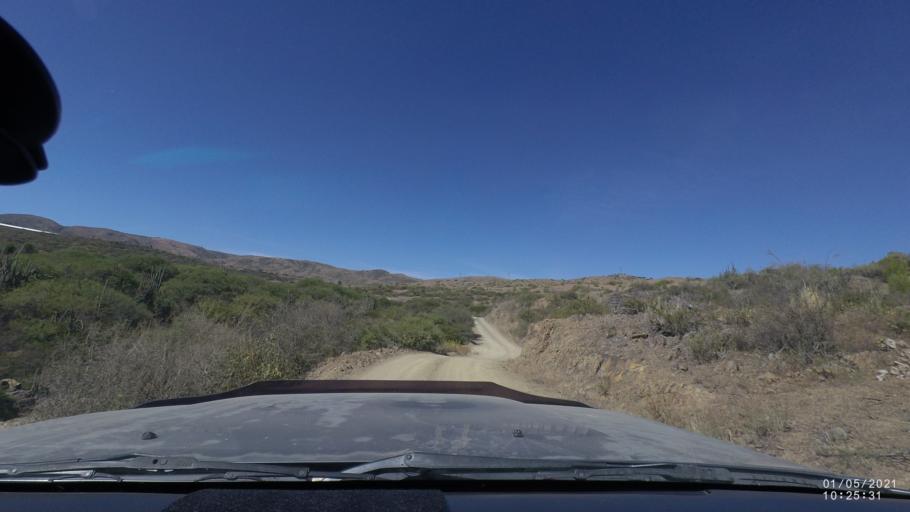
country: BO
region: Cochabamba
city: Capinota
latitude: -17.5783
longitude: -66.1933
